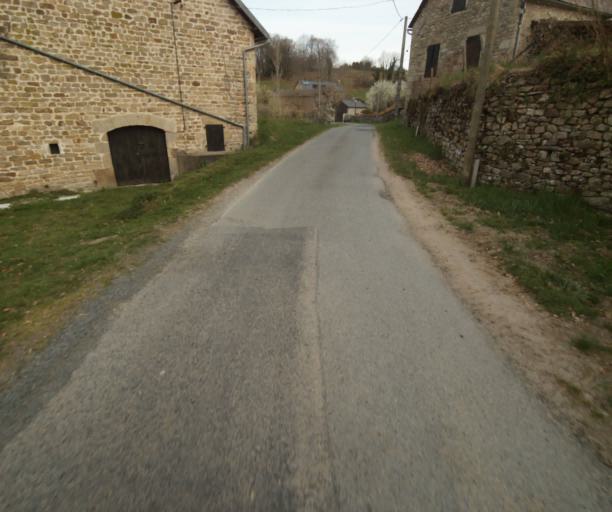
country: FR
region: Limousin
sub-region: Departement de la Correze
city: Correze
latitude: 45.4356
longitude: 1.8245
